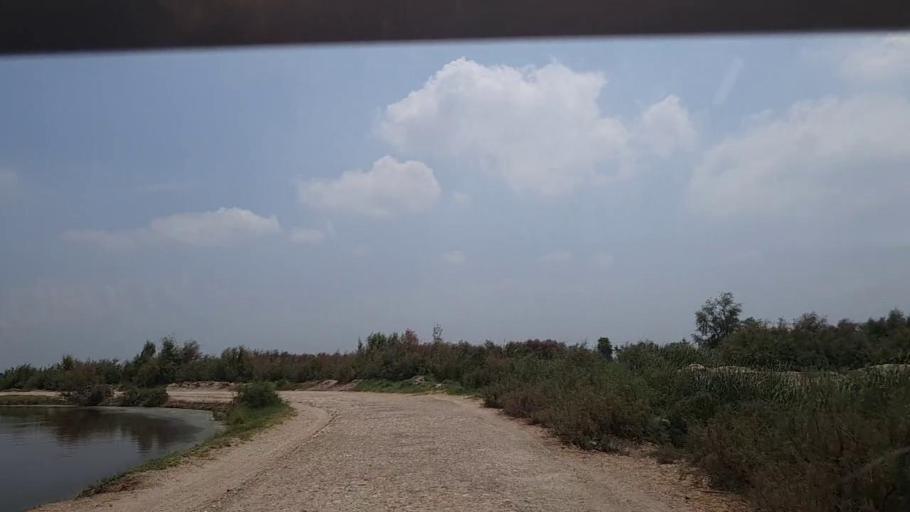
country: PK
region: Sindh
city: Khanpur
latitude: 27.8950
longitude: 69.3967
